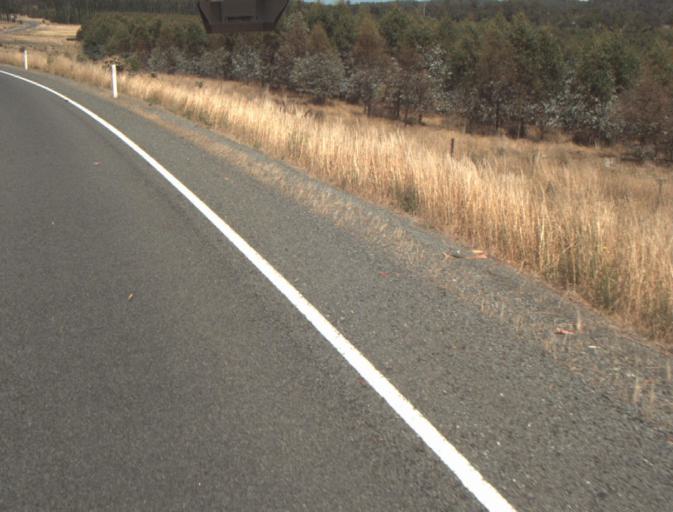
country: AU
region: Tasmania
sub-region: Launceston
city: Newstead
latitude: -41.3453
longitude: 147.3423
